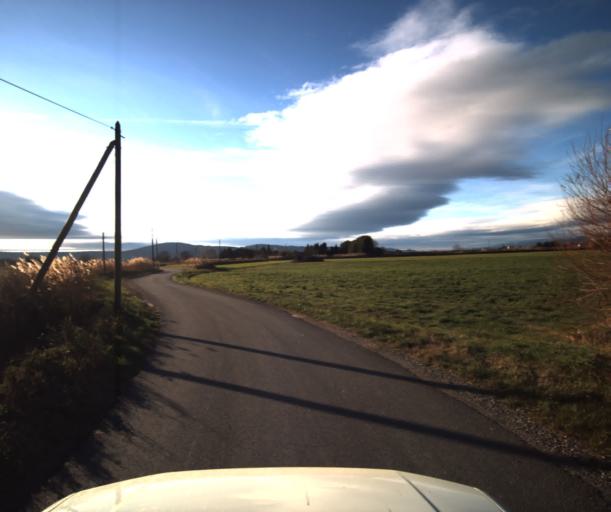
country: FR
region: Provence-Alpes-Cote d'Azur
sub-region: Departement du Vaucluse
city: Pertuis
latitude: 43.6932
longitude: 5.4647
